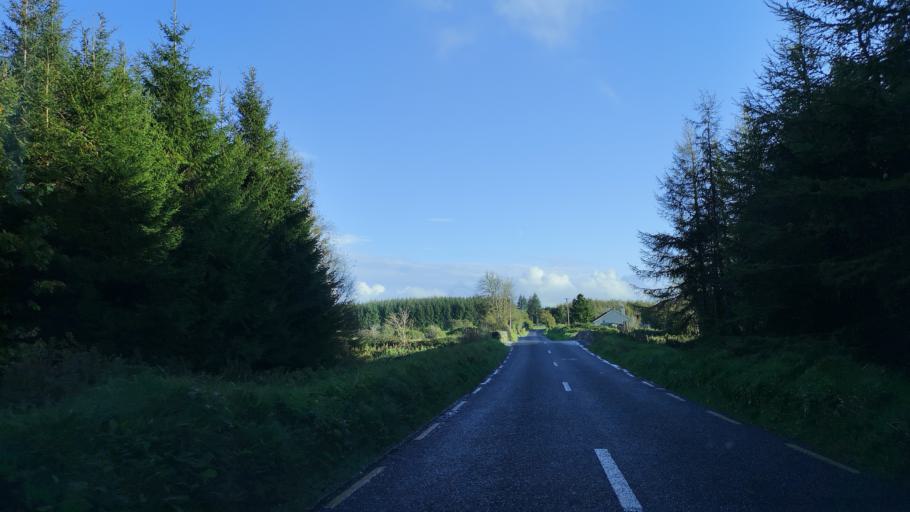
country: IE
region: Connaught
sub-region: Roscommon
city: Castlerea
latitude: 53.8048
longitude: -8.5050
